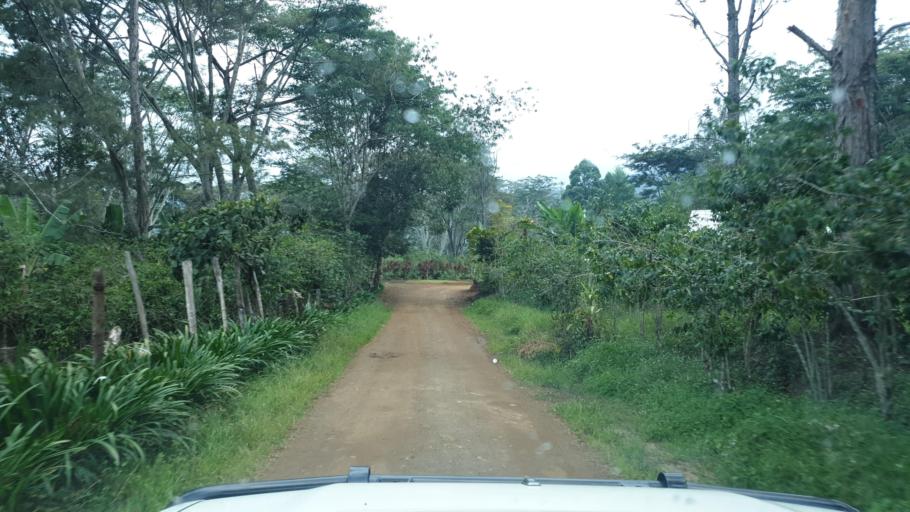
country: PG
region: Eastern Highlands
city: Goroka
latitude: -5.9564
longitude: 145.2725
